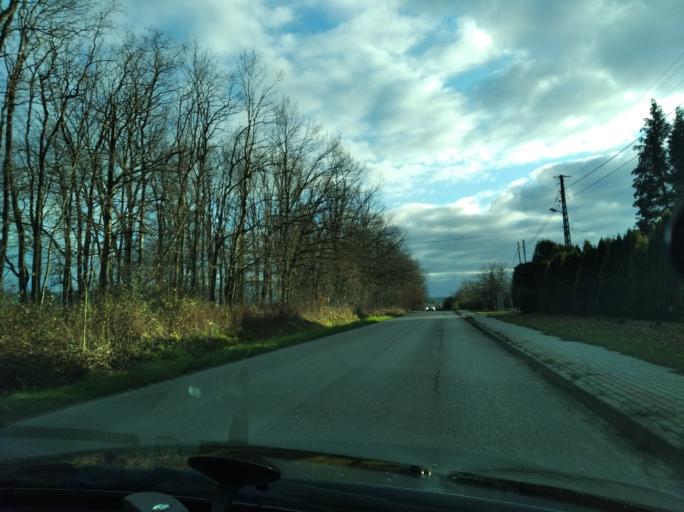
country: PL
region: Subcarpathian Voivodeship
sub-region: Powiat rzeszowski
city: Krasne
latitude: 50.0507
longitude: 22.1224
